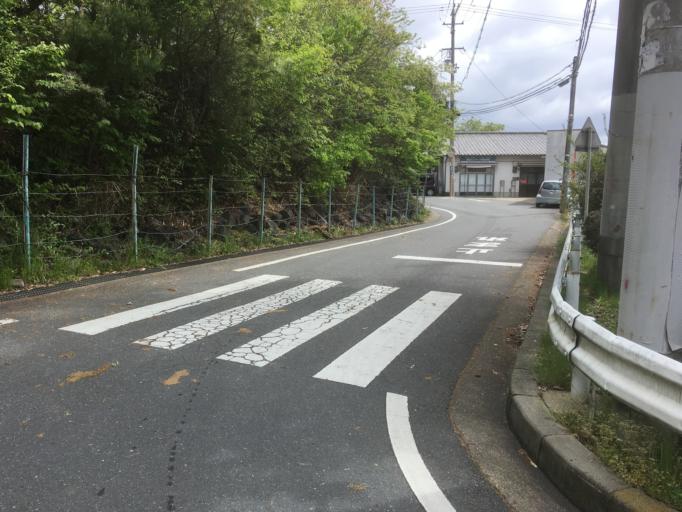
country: JP
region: Nara
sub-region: Ikoma-shi
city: Ikoma
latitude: 34.6998
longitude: 135.6913
